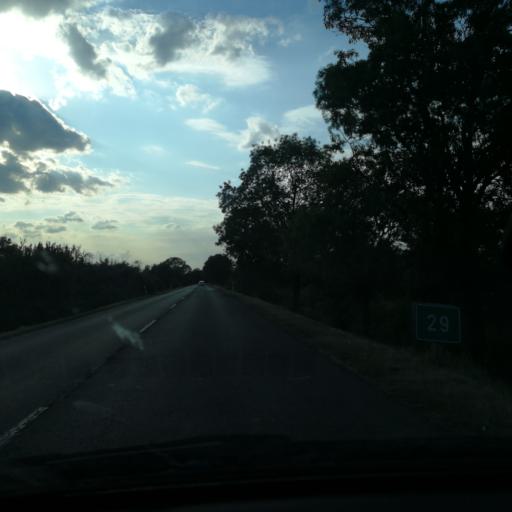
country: HU
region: Csongrad
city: Csongrad
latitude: 46.6865
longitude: 20.1743
